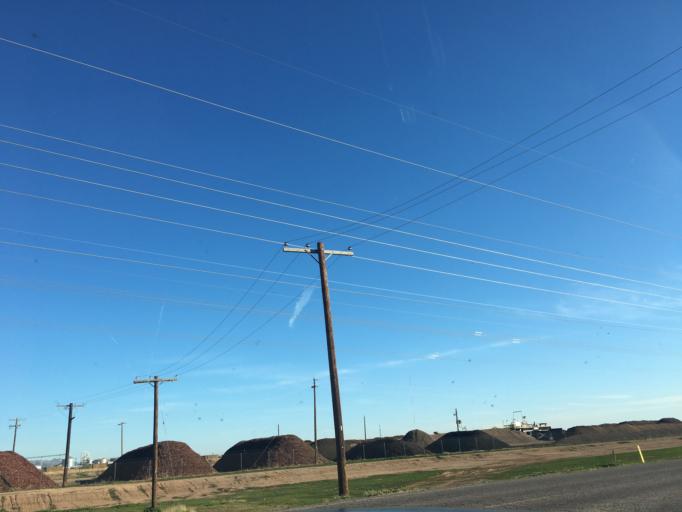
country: US
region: Arizona
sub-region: Pinal County
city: Maricopa
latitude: 33.0143
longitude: -111.9966
